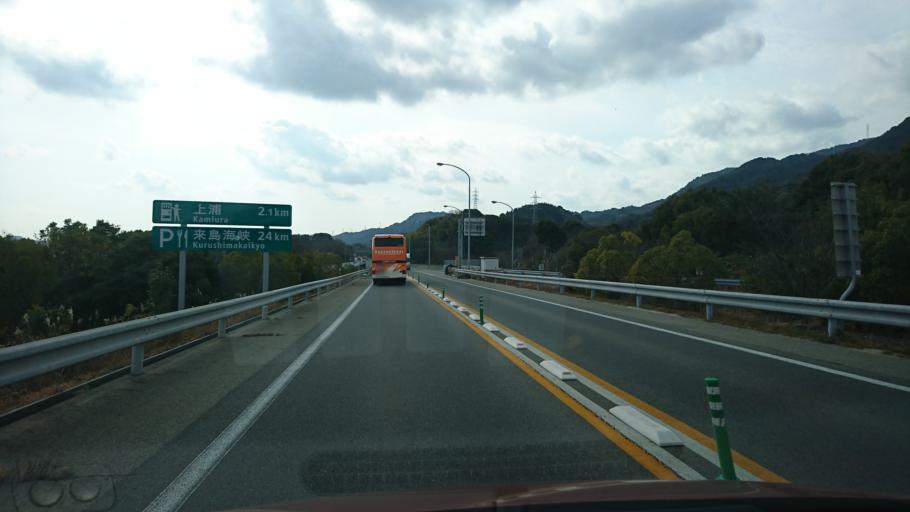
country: JP
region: Hiroshima
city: Innoshima
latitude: 34.2503
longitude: 133.0490
